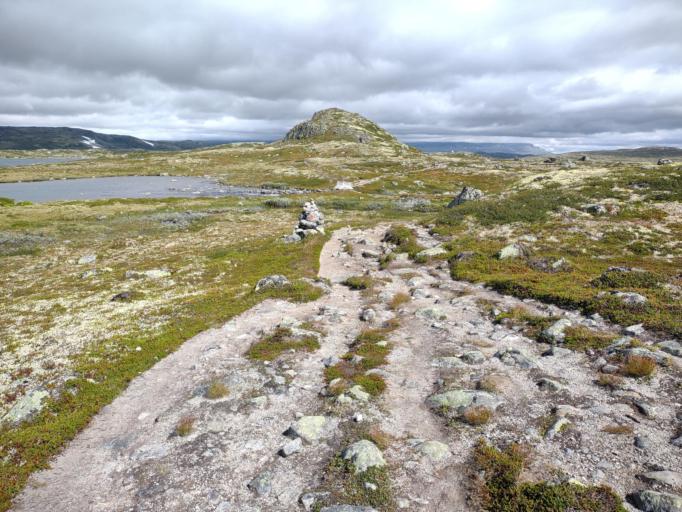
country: NO
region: Buskerud
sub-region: Hol
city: Geilo
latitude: 60.4492
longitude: 7.7009
